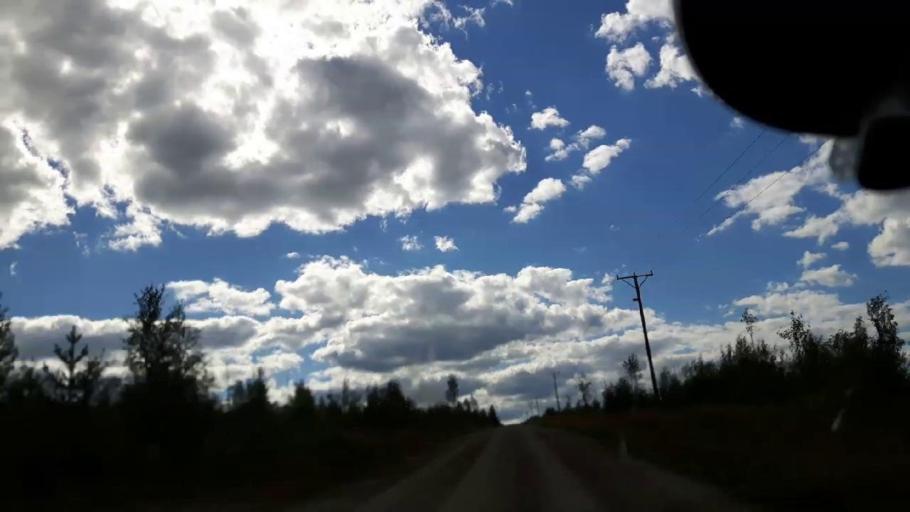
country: SE
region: Vaesternorrland
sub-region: Ange Kommun
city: Ange
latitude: 62.7606
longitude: 15.6873
